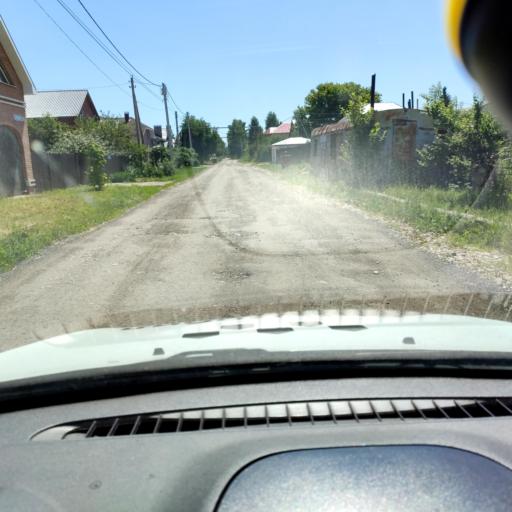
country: RU
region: Samara
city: Tol'yatti
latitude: 53.5679
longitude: 49.3866
